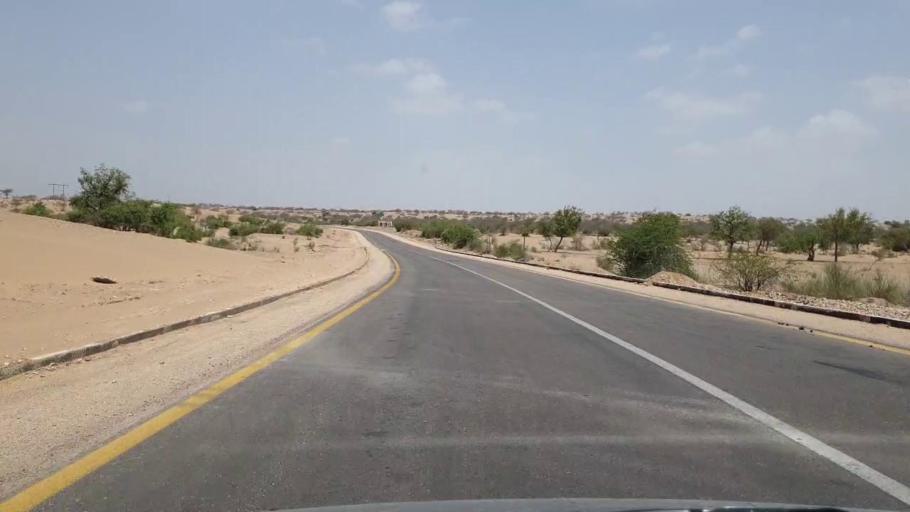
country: PK
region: Sindh
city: Mithi
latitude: 24.8193
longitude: 69.7019
